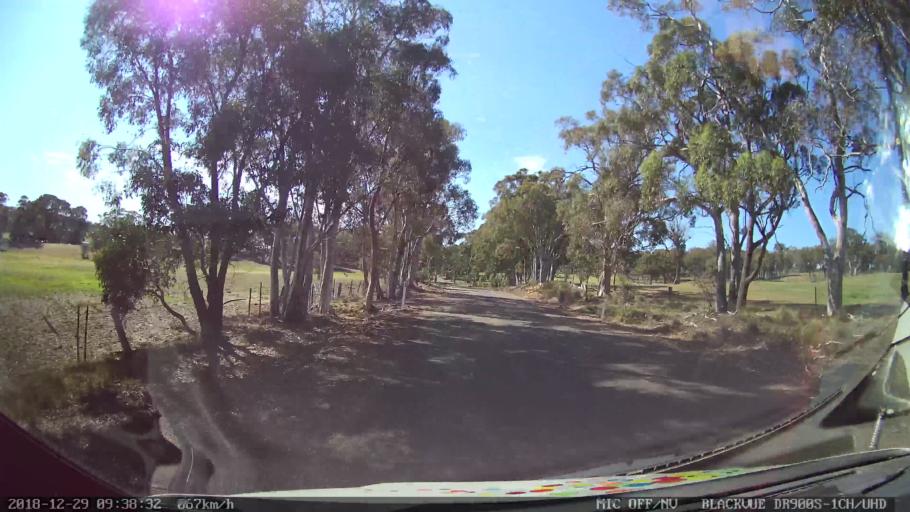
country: AU
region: New South Wales
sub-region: Upper Lachlan Shire
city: Crookwell
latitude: -34.6478
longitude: 149.3766
